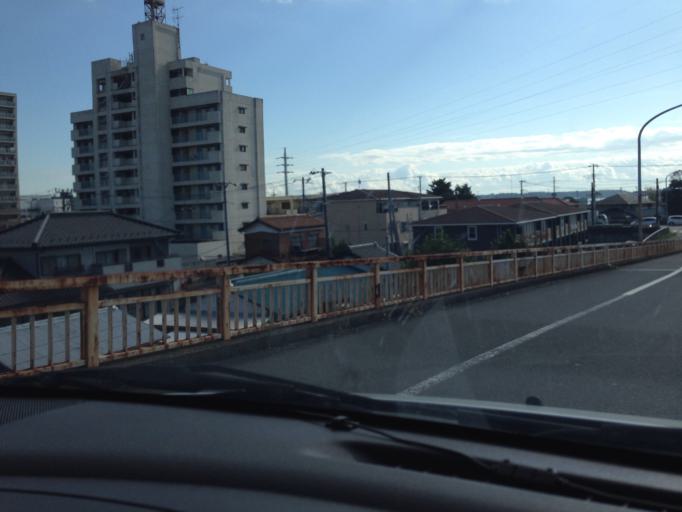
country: JP
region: Ibaraki
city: Ami
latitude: 36.0828
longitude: 140.2093
